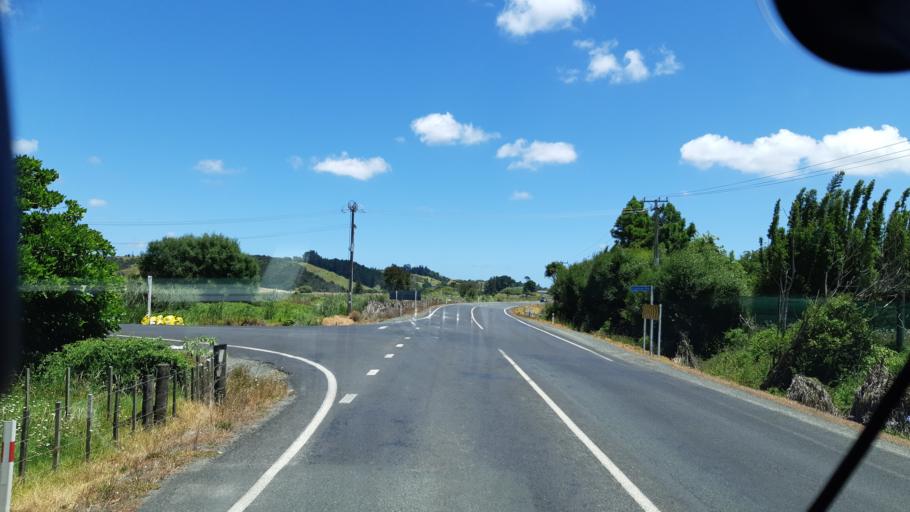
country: NZ
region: Northland
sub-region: Far North District
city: Kaitaia
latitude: -35.1245
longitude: 173.2878
